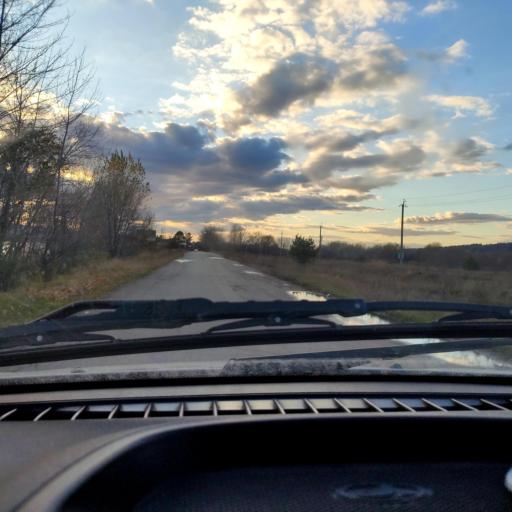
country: RU
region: Samara
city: Povolzhskiy
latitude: 53.4652
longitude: 49.6764
